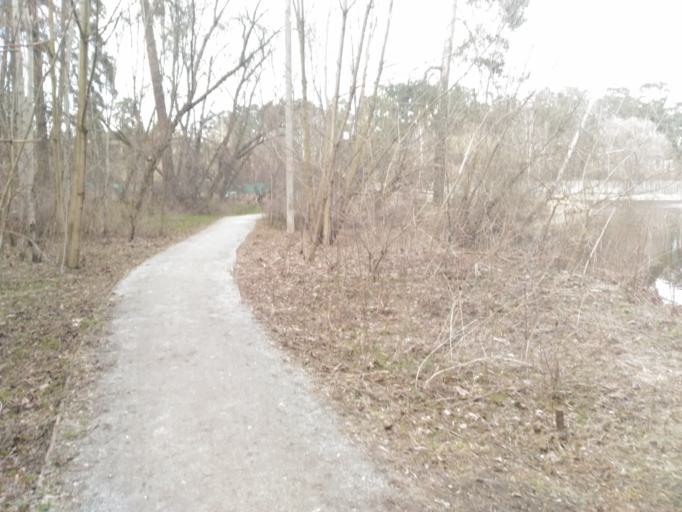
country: RU
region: Moscow
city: Shchukino
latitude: 55.7815
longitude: 37.4270
